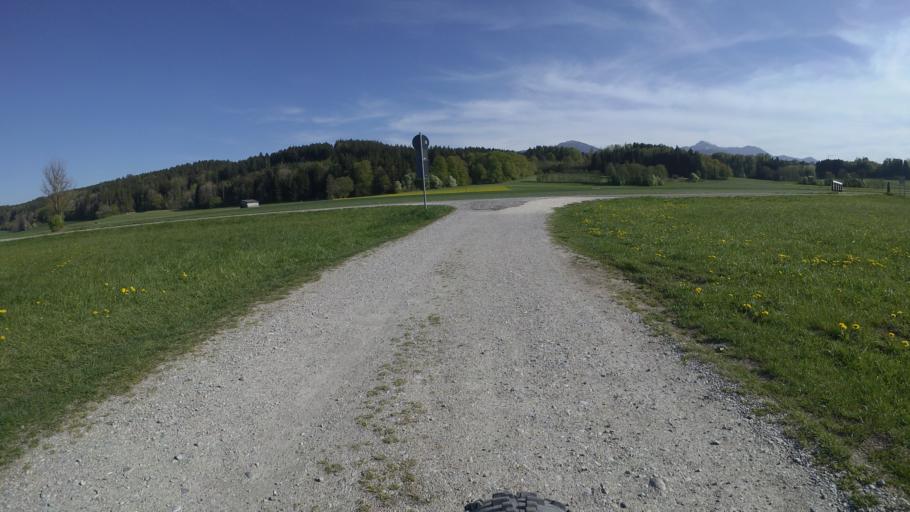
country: DE
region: Bavaria
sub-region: Upper Bavaria
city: Grabenstatt
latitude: 47.8448
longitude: 12.5577
